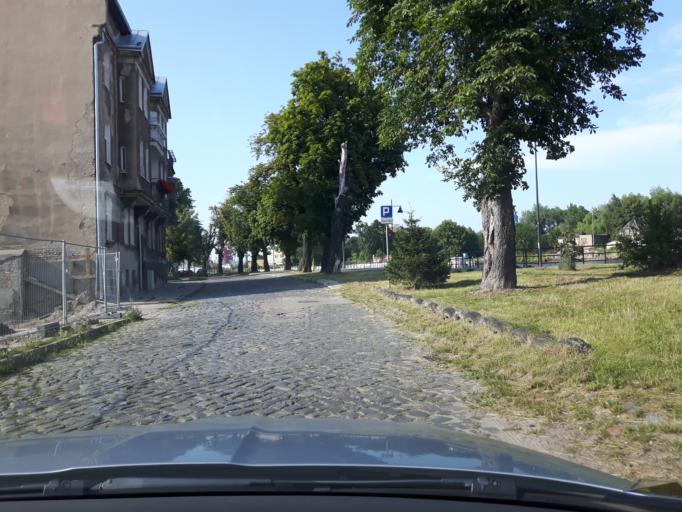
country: PL
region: Pomeranian Voivodeship
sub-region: Gdansk
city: Gdansk
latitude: 54.3568
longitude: 18.6656
